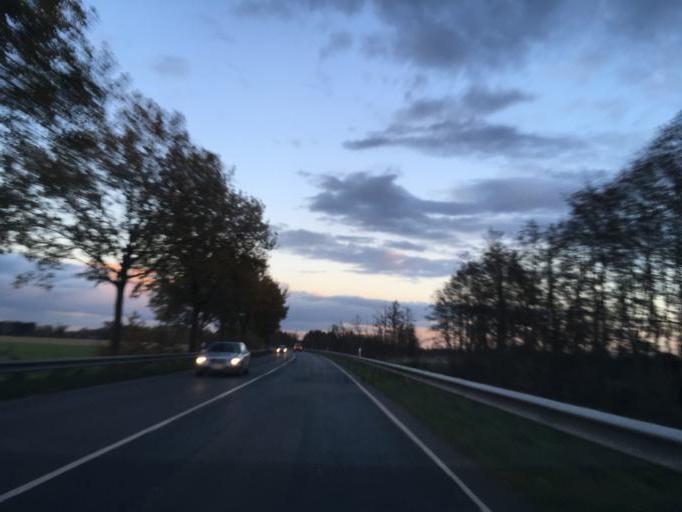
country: DE
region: Lower Saxony
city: Winsen
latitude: 53.3554
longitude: 10.1609
